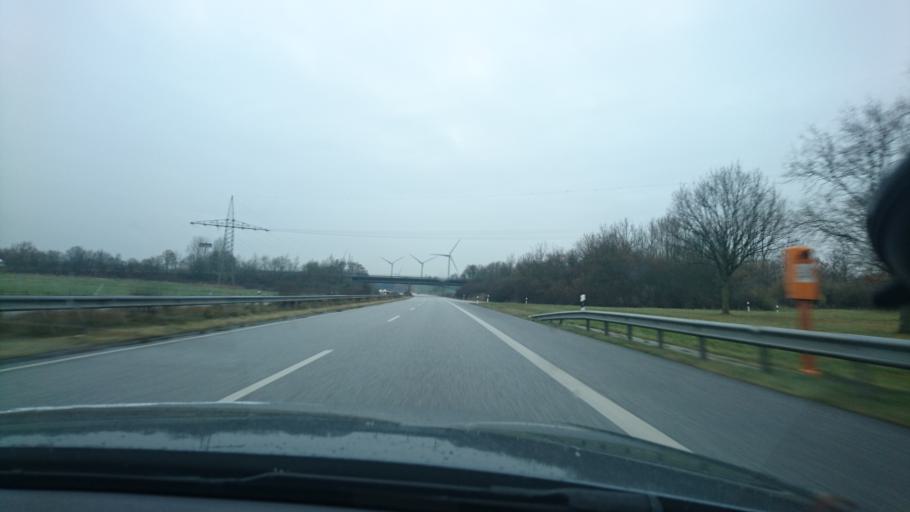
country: DE
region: Schleswig-Holstein
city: Kabelhorst
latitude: 54.2142
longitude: 10.9020
